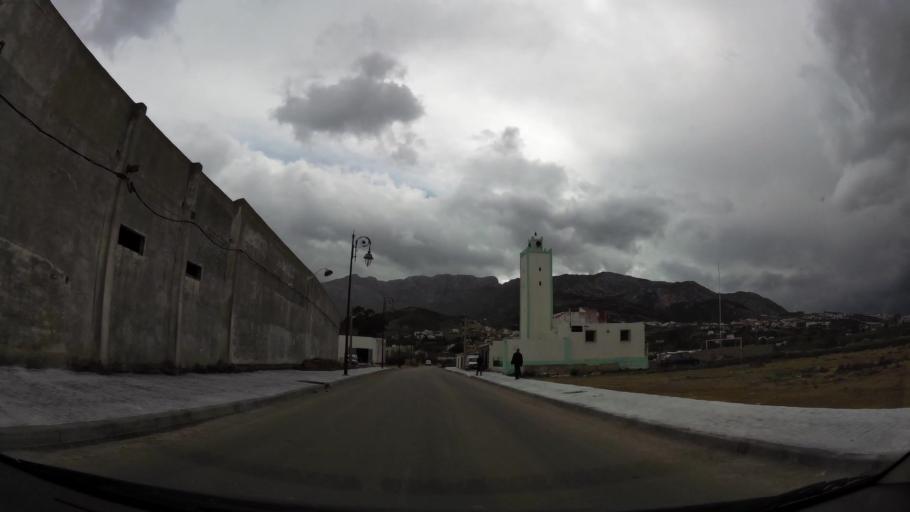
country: MA
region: Tanger-Tetouan
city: Tetouan
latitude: 35.5572
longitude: -5.3523
